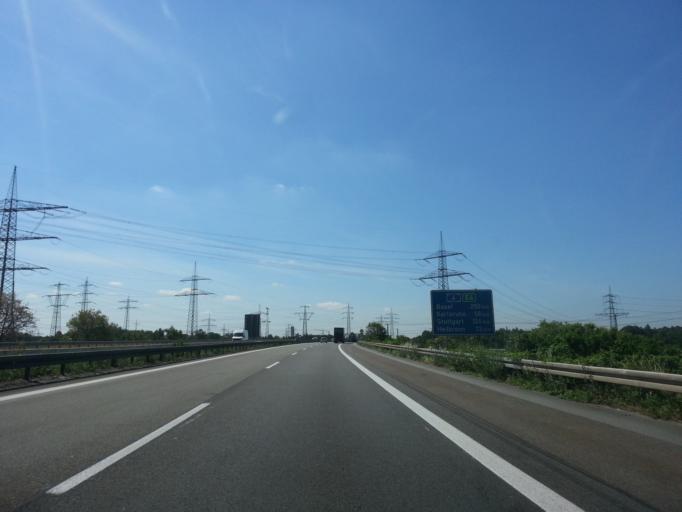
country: DE
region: Baden-Wuerttemberg
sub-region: Karlsruhe Region
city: Ilvesheim
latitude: 49.4531
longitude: 8.5421
